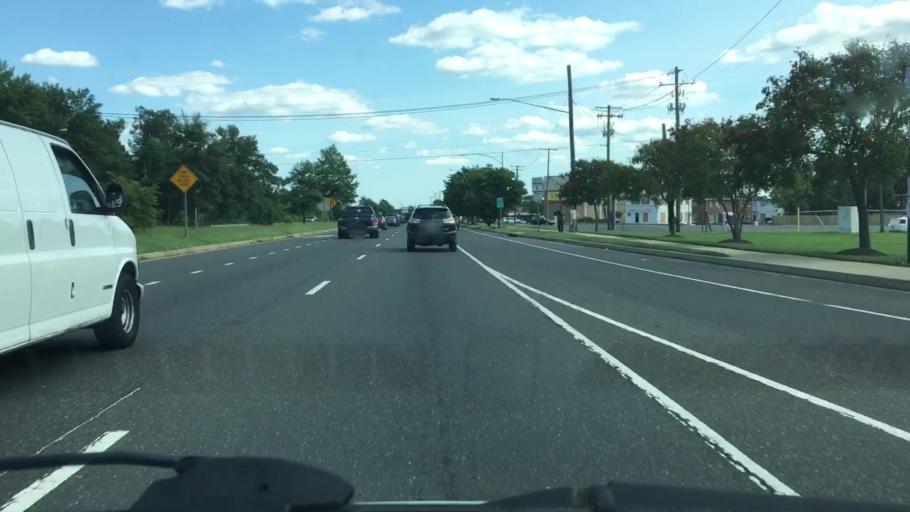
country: US
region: Maryland
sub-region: Prince George's County
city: Silver Hill
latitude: 38.8390
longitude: -76.9463
